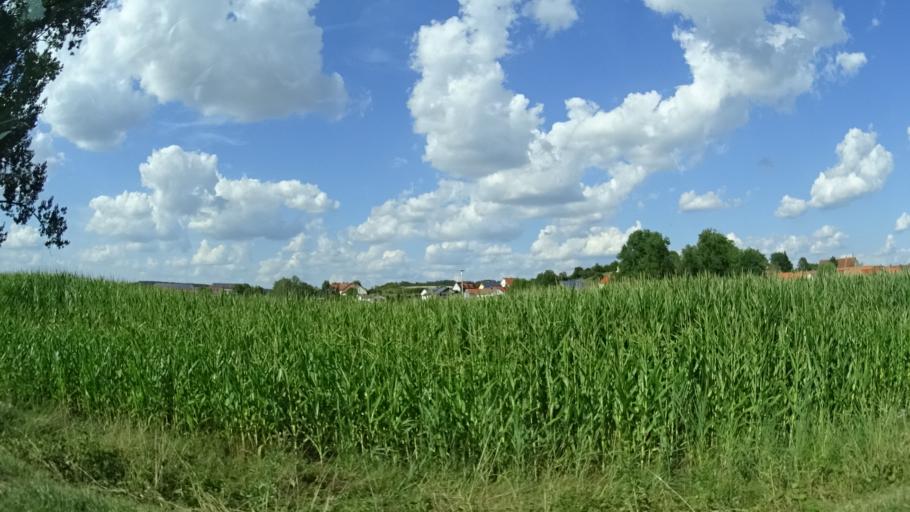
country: DE
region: Bavaria
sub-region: Regierungsbezirk Unterfranken
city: Bundorf
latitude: 50.2669
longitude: 10.5338
